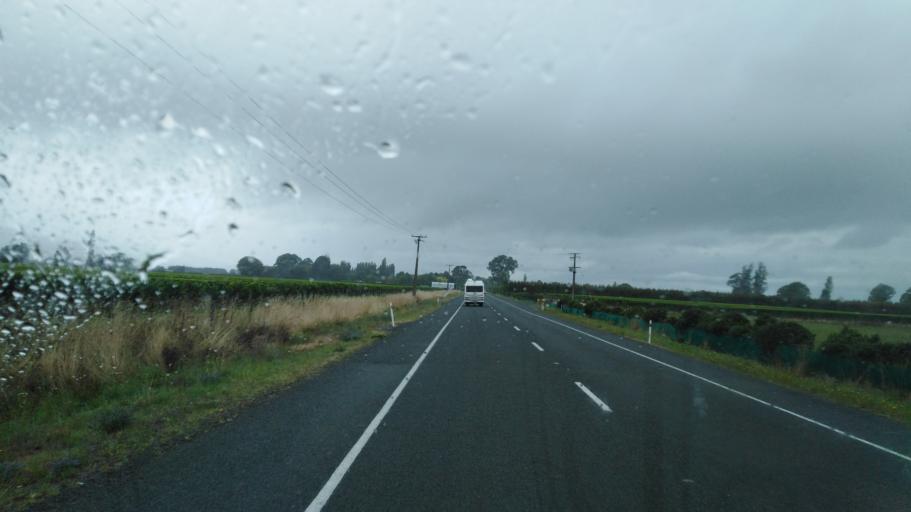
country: NZ
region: Marlborough
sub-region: Marlborough District
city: Blenheim
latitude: -41.4608
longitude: 173.9410
